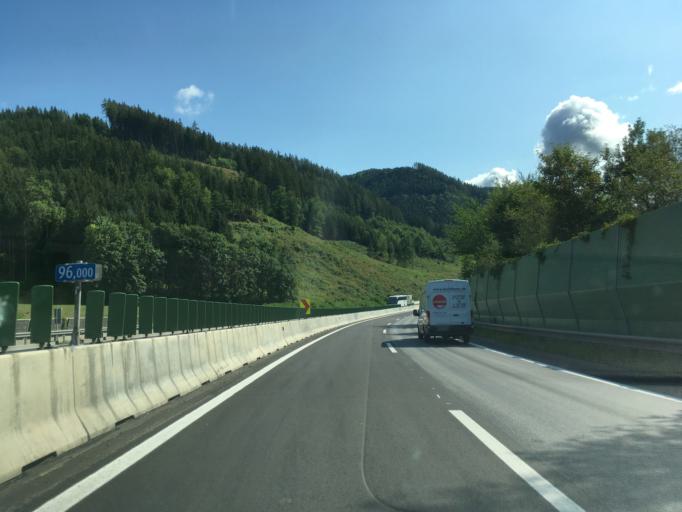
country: AT
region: Styria
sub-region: Politischer Bezirk Leoben
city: Leoben
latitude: 47.3616
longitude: 15.1080
